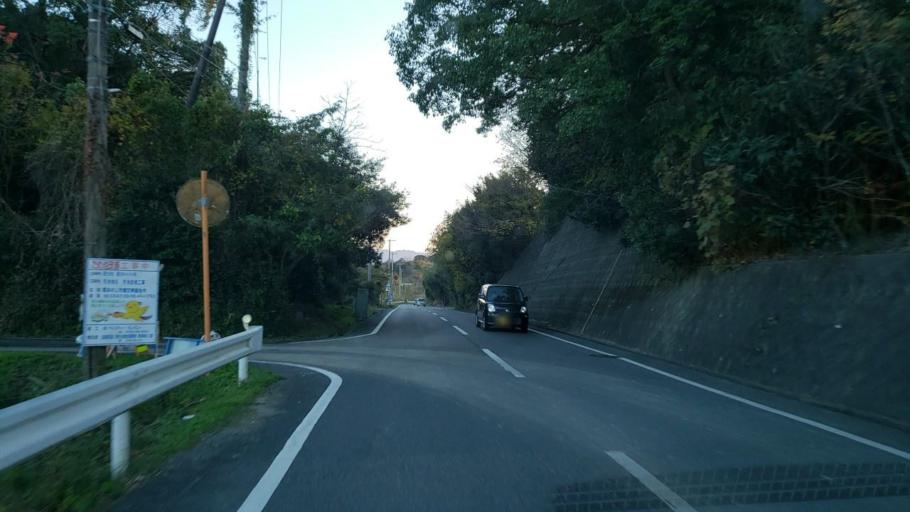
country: JP
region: Hyogo
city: Fukura
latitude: 34.3452
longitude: 134.7825
